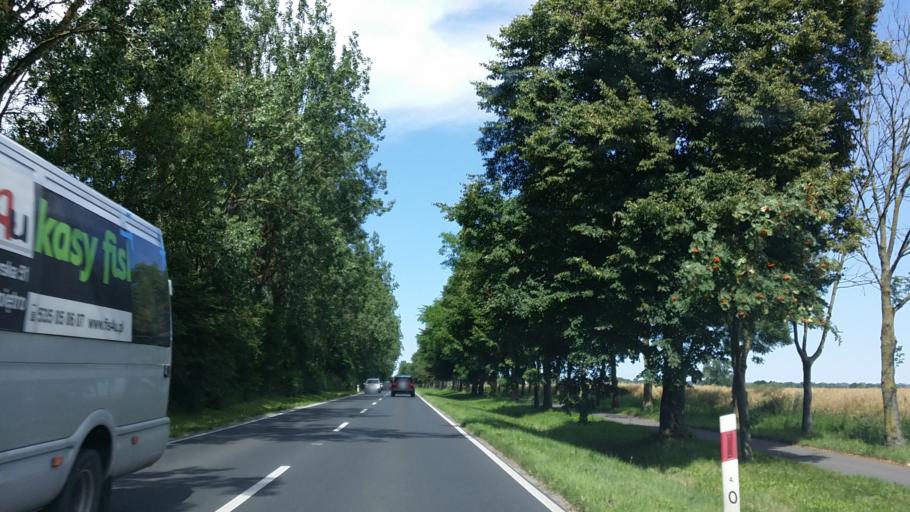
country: PL
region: West Pomeranian Voivodeship
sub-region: Powiat koszalinski
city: Mielno
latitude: 54.2237
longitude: 16.0763
